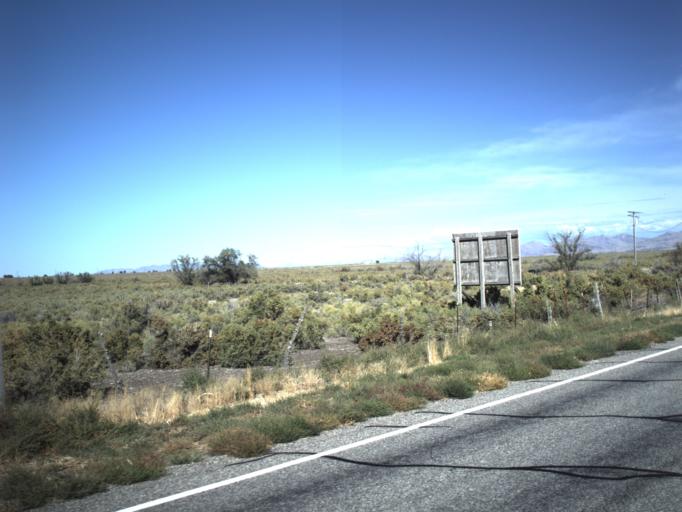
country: US
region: Utah
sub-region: Millard County
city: Delta
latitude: 39.3528
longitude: -112.5400
